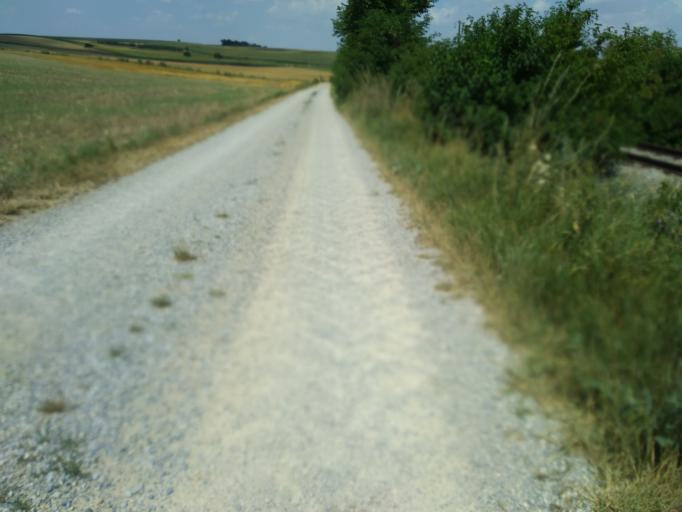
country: AT
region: Lower Austria
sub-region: Politischer Bezirk Ganserndorf
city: Bad Pirawarth
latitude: 48.4549
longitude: 16.6103
